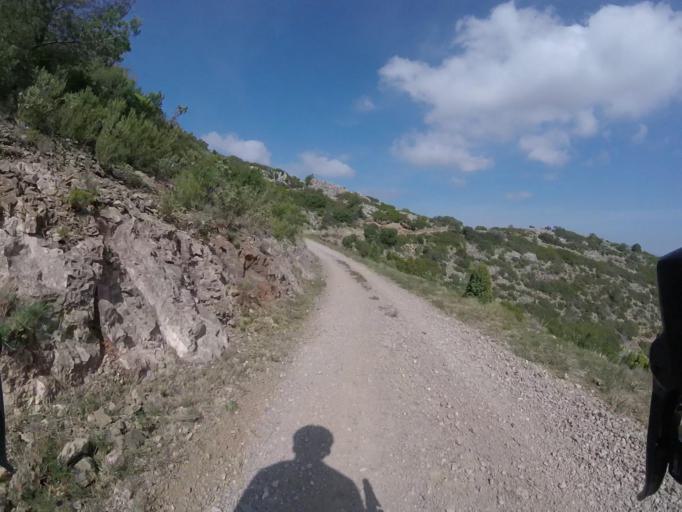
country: ES
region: Valencia
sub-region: Provincia de Castello
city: Benicassim
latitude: 40.0987
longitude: 0.0459
